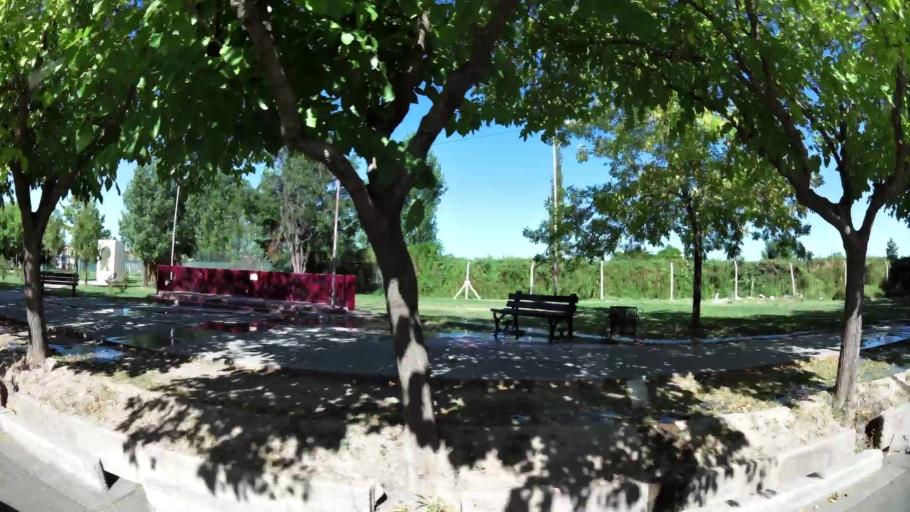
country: AR
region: Mendoza
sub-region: Departamento de Godoy Cruz
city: Godoy Cruz
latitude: -32.9484
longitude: -68.8125
